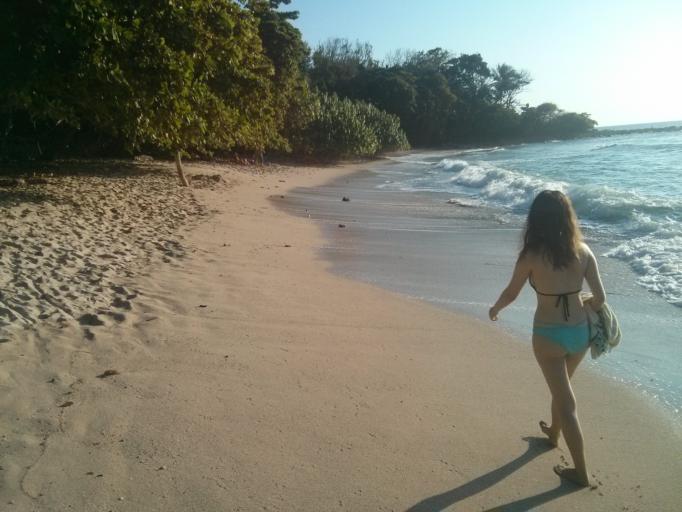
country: CR
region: Puntarenas
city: Paquera
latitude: 9.5943
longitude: -85.1429
